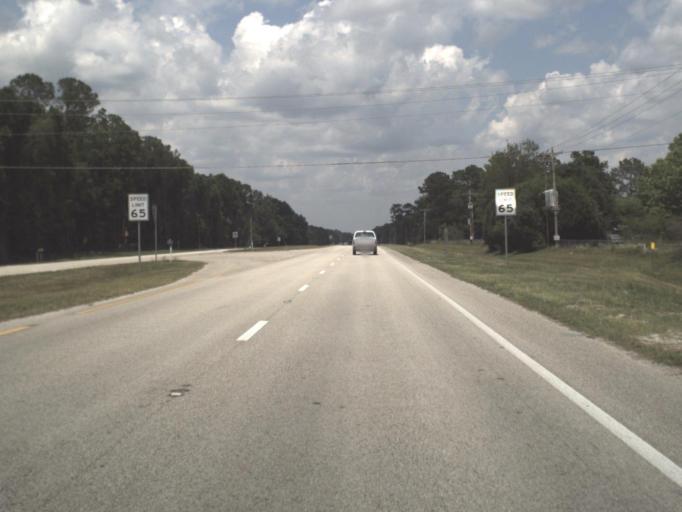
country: US
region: Florida
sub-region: Alachua County
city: Gainesville
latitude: 29.7249
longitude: -82.2565
